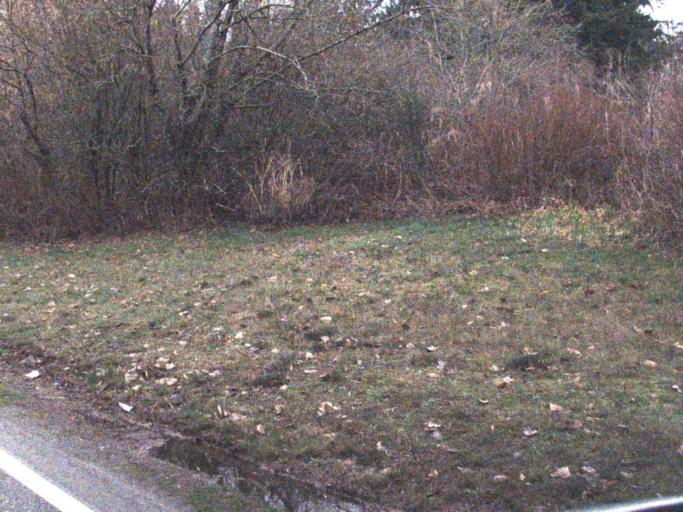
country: US
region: Washington
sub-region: Snohomish County
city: Smokey Point
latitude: 48.1519
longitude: -122.2224
